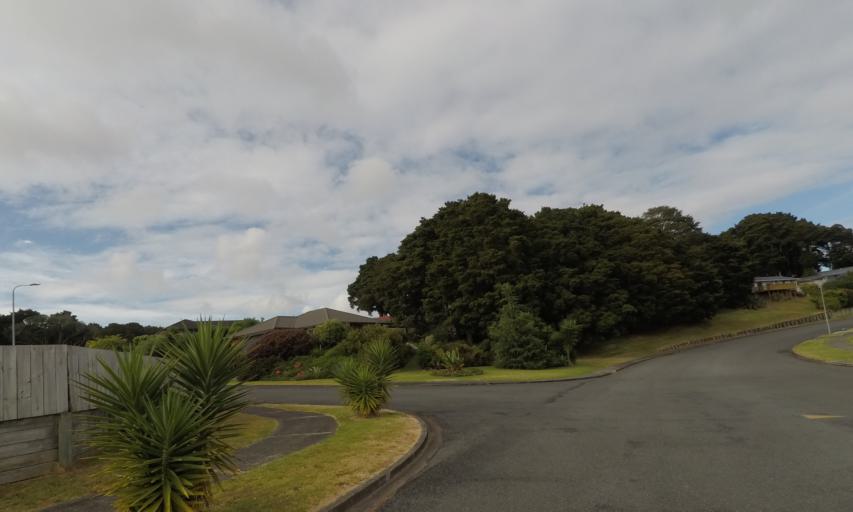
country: NZ
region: Northland
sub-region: Whangarei
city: Whangarei
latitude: -35.6729
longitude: 174.3143
